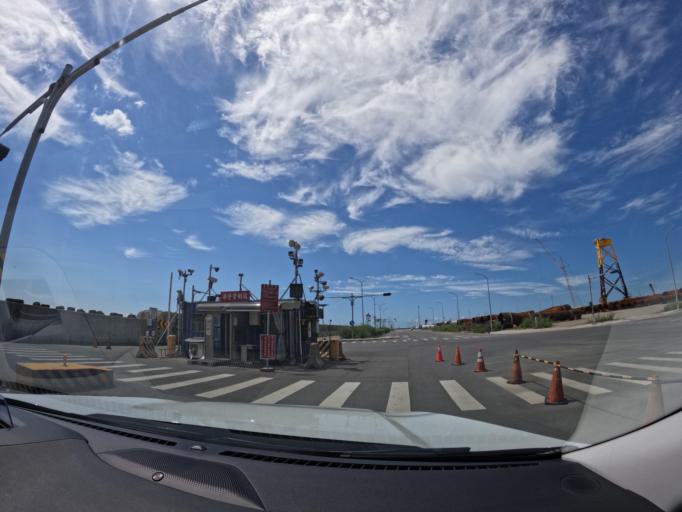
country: TW
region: Taiwan
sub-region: Taoyuan
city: Taoyuan
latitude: 25.1414
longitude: 121.3658
